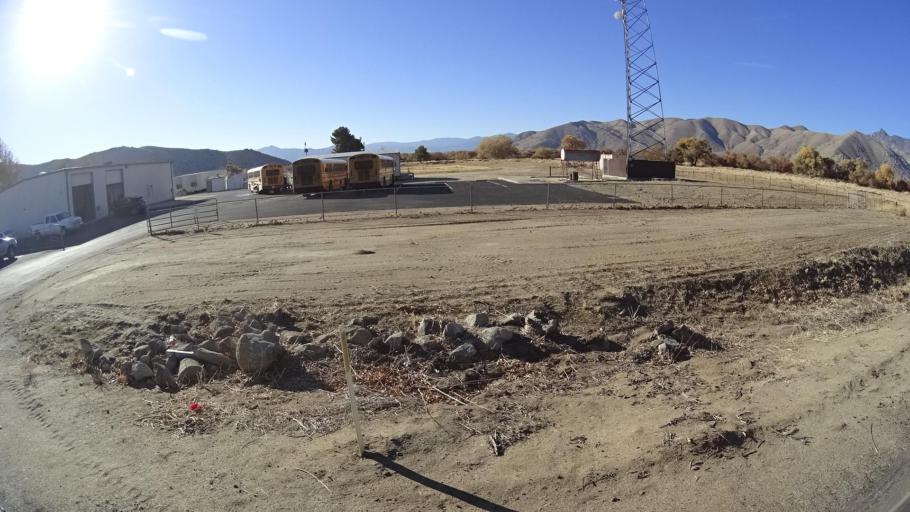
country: US
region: California
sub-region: Kern County
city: Weldon
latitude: 35.6673
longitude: -118.2900
